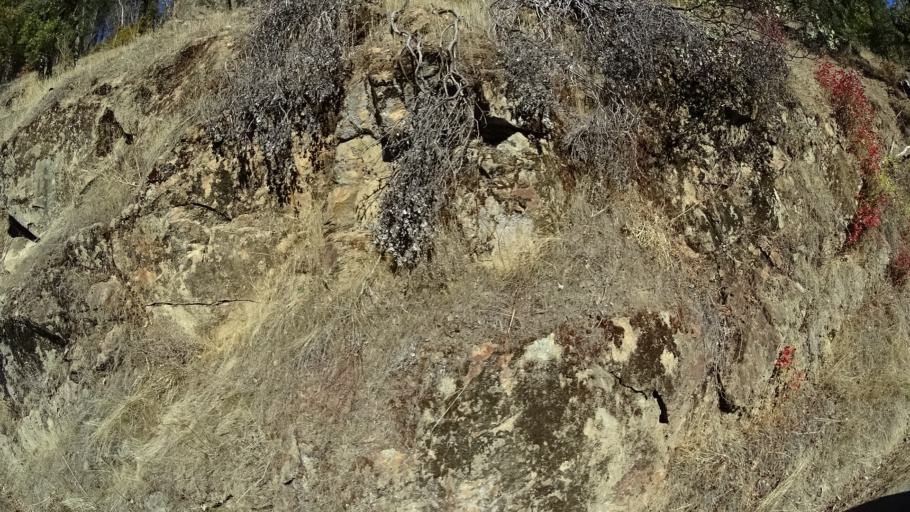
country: US
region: California
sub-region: Siskiyou County
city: Happy Camp
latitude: 41.3172
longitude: -123.1693
